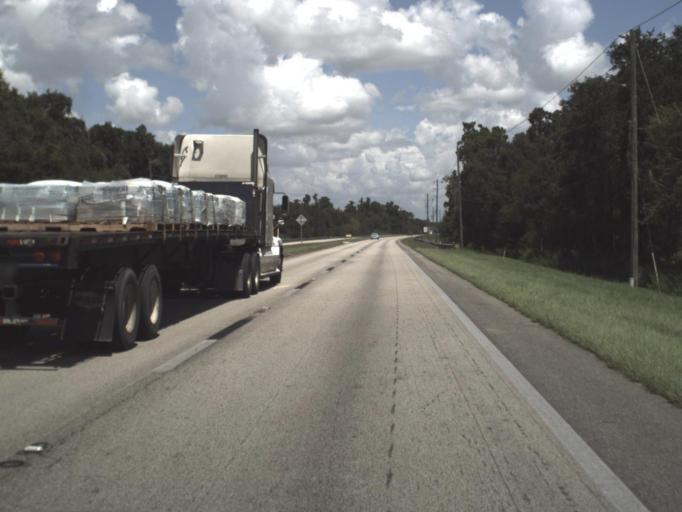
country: US
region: Florida
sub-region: Polk County
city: Bartow
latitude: 27.9157
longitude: -81.8258
